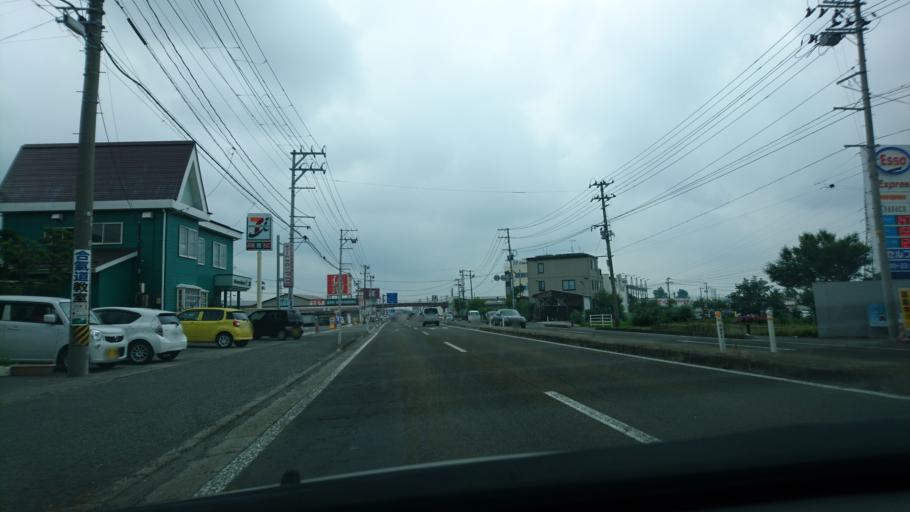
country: JP
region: Miyagi
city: Furukawa
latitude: 38.5856
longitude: 140.9457
